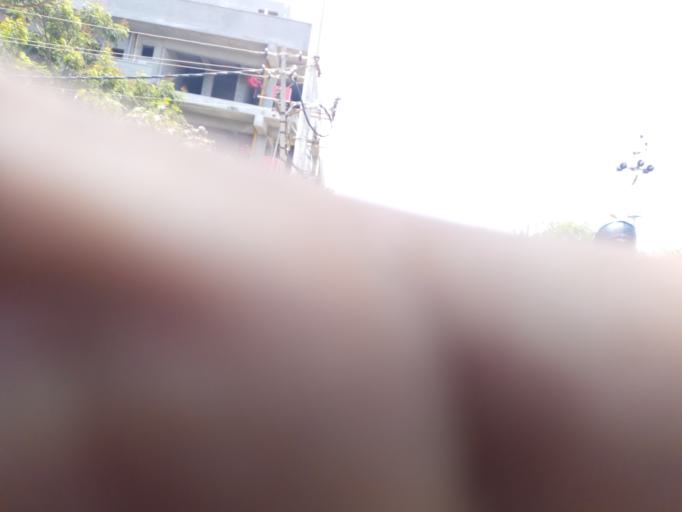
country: IN
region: Karnataka
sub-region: Bangalore Urban
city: Bangalore
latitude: 12.8814
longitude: 77.6553
